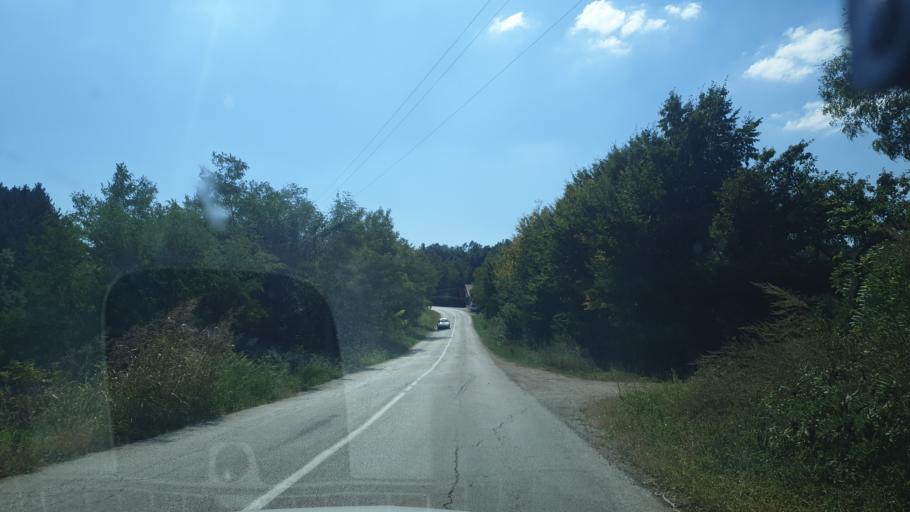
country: RS
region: Central Serbia
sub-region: Zlatiborski Okrug
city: Kosjeric
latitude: 43.9871
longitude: 20.0419
